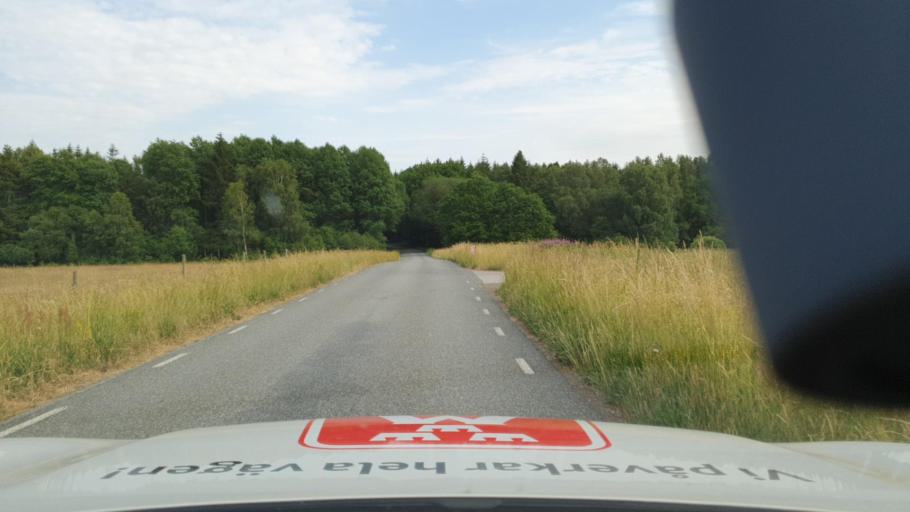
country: SE
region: Skane
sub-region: Kristianstads Kommun
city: Degeberga
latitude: 55.6960
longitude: 14.0638
